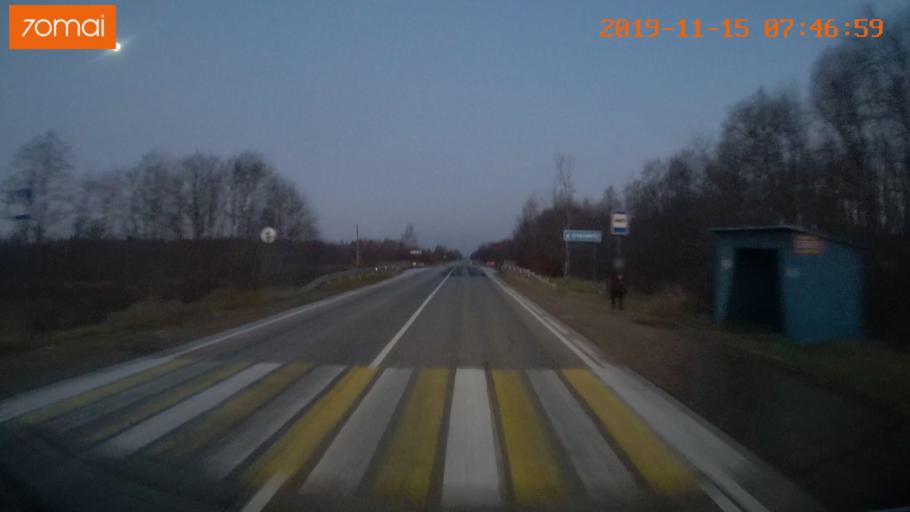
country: RU
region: Vologda
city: Sheksna
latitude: 58.8374
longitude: 38.2689
